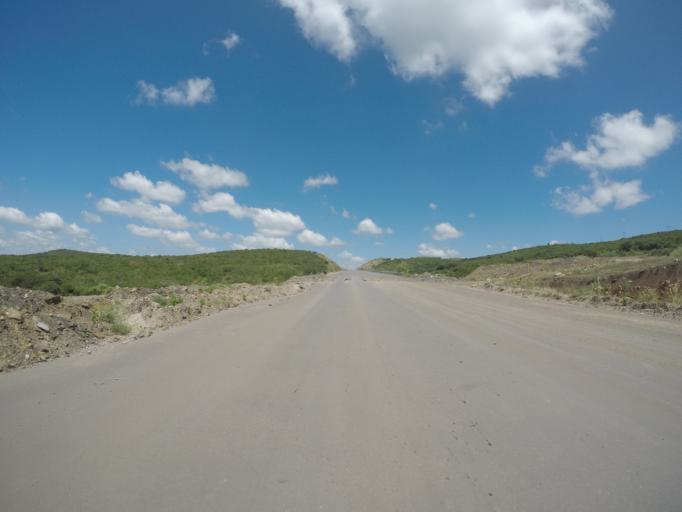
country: ZA
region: KwaZulu-Natal
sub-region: uThungulu District Municipality
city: Empangeni
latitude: -28.6235
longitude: 31.7576
